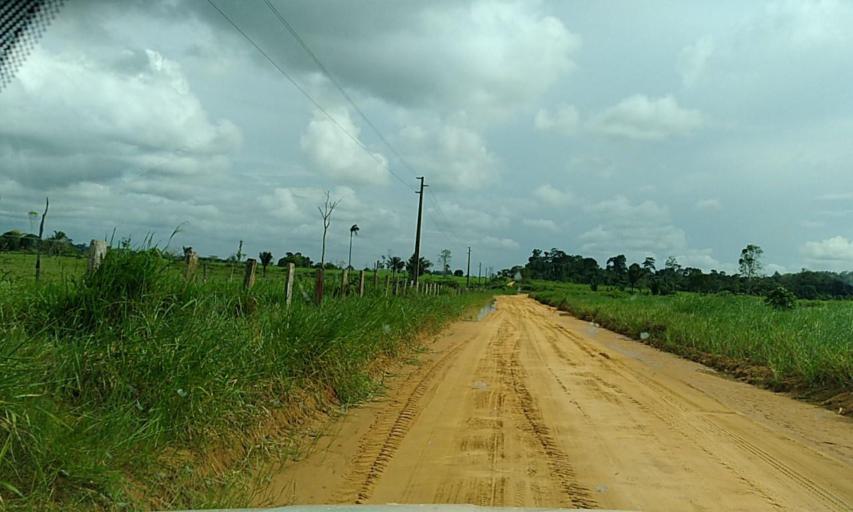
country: BR
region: Para
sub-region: Altamira
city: Altamira
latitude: -3.2309
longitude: -52.6955
